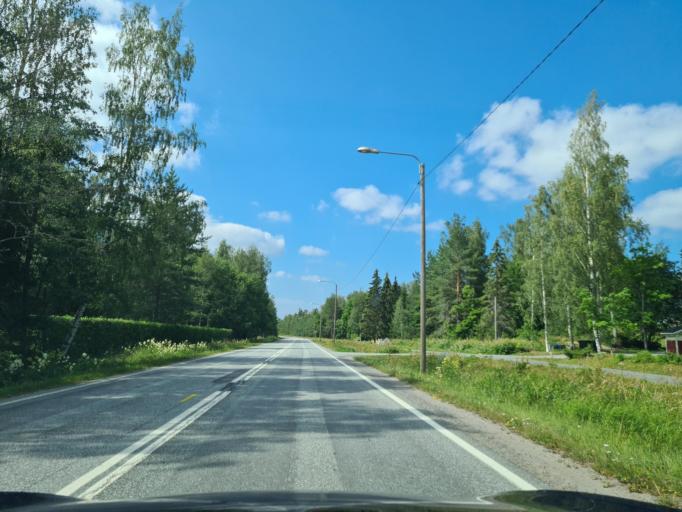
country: FI
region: Ostrobothnia
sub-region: Vaasa
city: Vaasa
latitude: 63.1935
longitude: 21.5569
